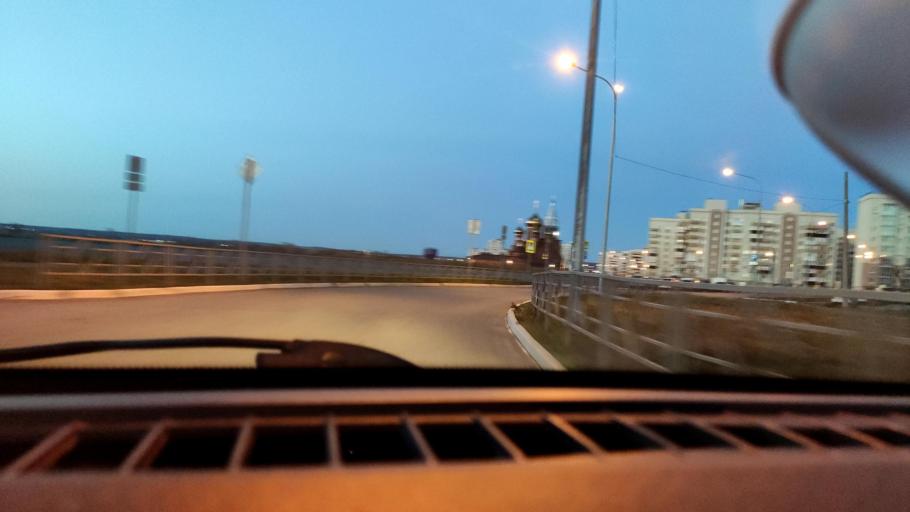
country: RU
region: Samara
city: Samara
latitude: 53.1136
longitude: 50.1532
